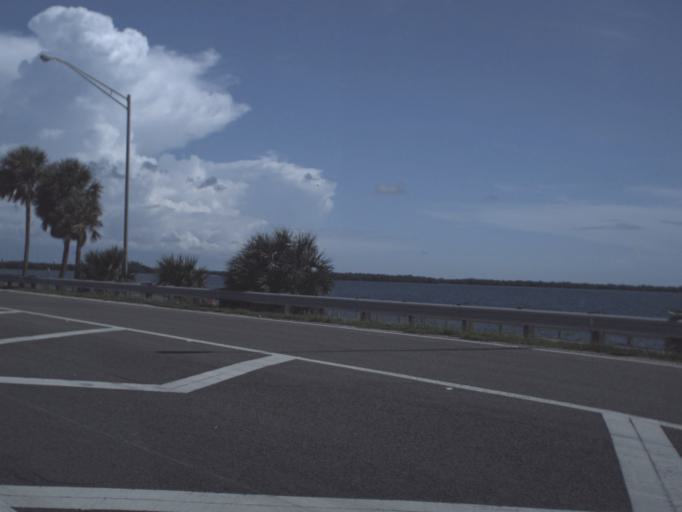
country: US
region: Florida
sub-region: Manatee County
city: Memphis
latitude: 27.5850
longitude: -82.6174
